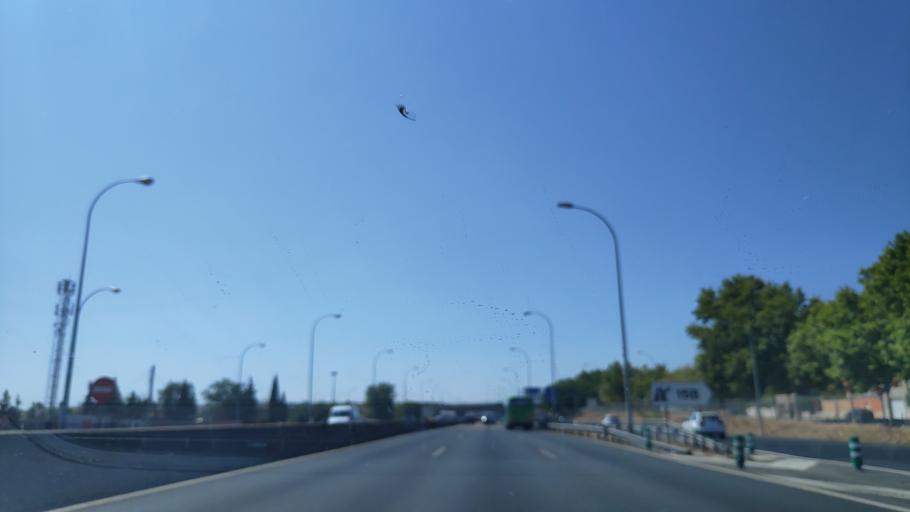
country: ES
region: Madrid
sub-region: Provincia de Madrid
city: Getafe
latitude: 40.2831
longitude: -3.7460
